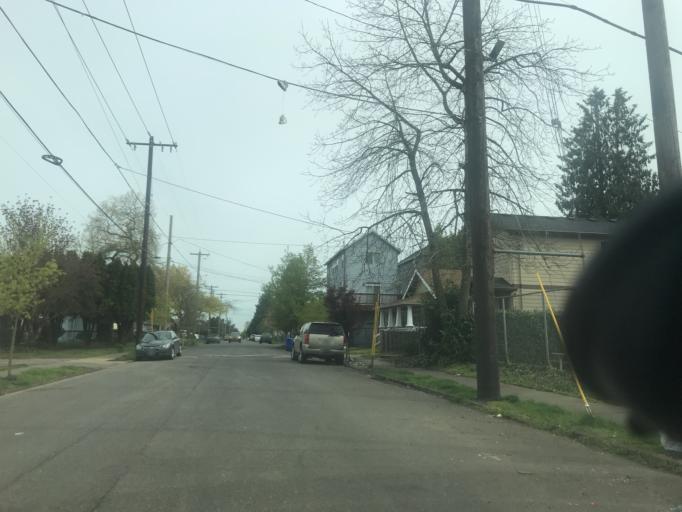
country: US
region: Oregon
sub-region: Multnomah County
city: Lents
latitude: 45.4908
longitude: -122.5811
